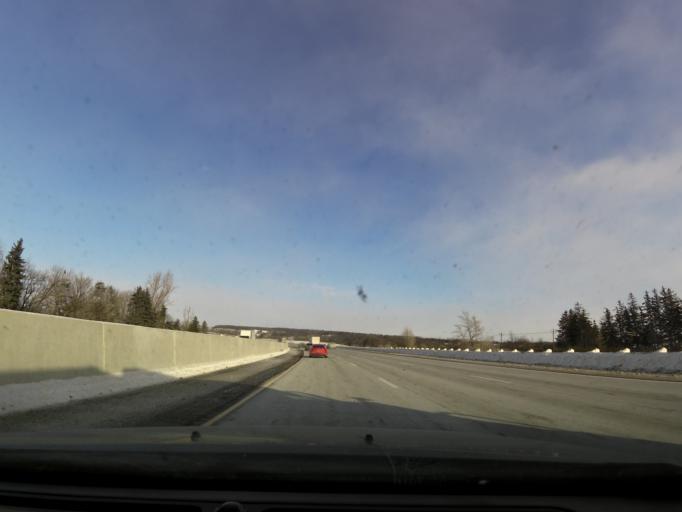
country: CA
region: Ontario
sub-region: Halton
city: Milton
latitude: 43.4959
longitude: -79.9673
